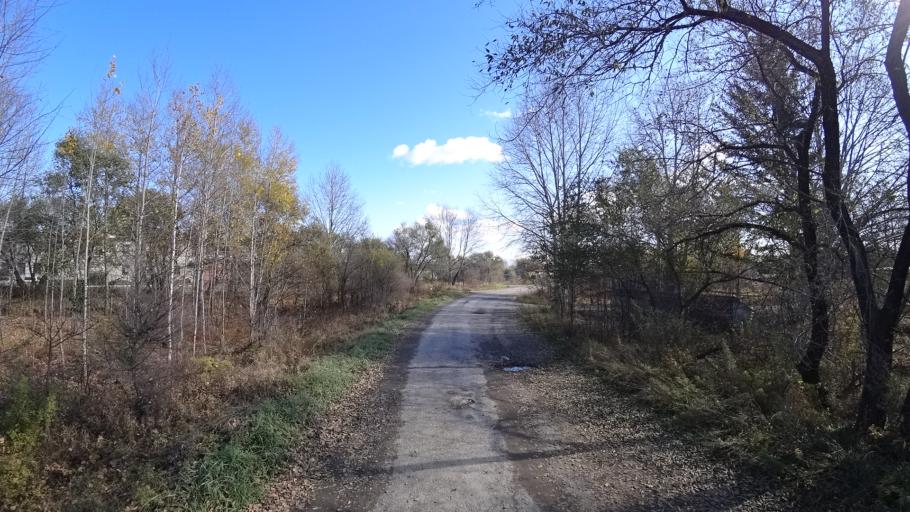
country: RU
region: Khabarovsk Krai
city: Amursk
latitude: 50.1024
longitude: 136.5043
